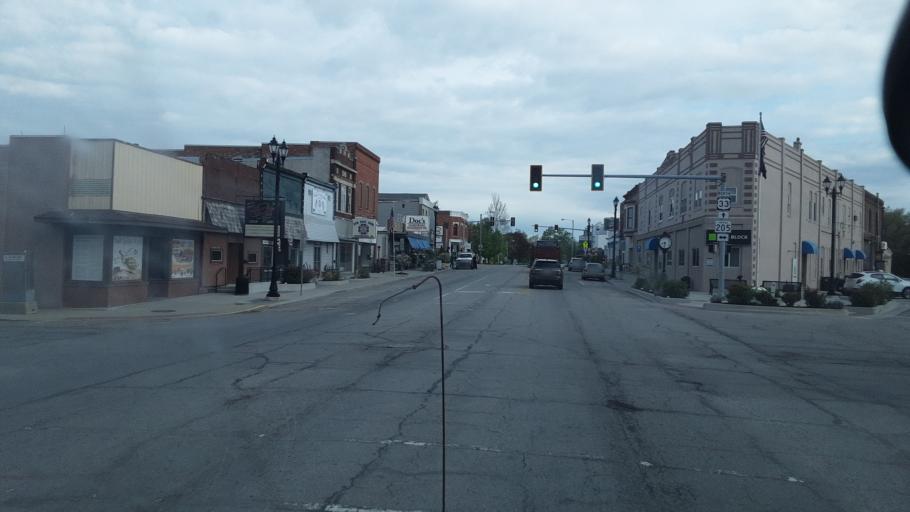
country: US
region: Indiana
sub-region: Whitley County
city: Churubusco
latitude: 41.2304
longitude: -85.3192
